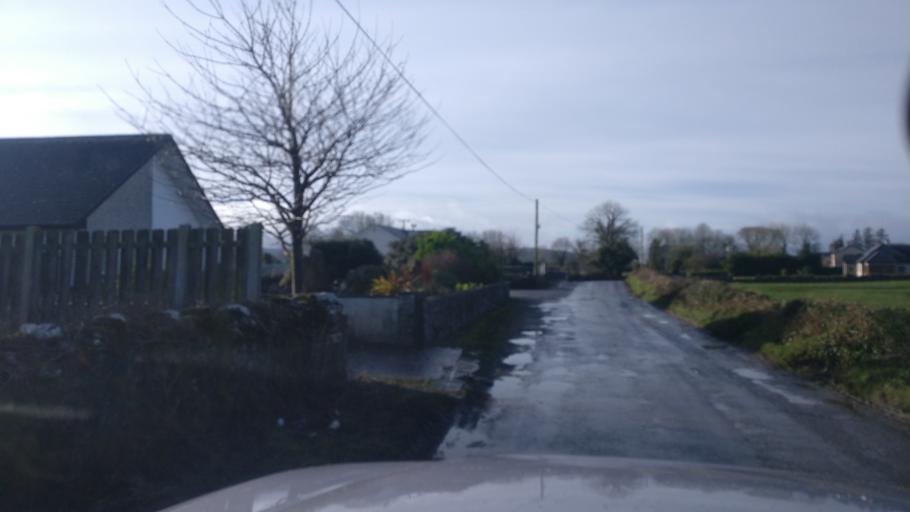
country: IE
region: Connaught
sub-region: County Galway
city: Loughrea
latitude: 53.1969
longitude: -8.6167
